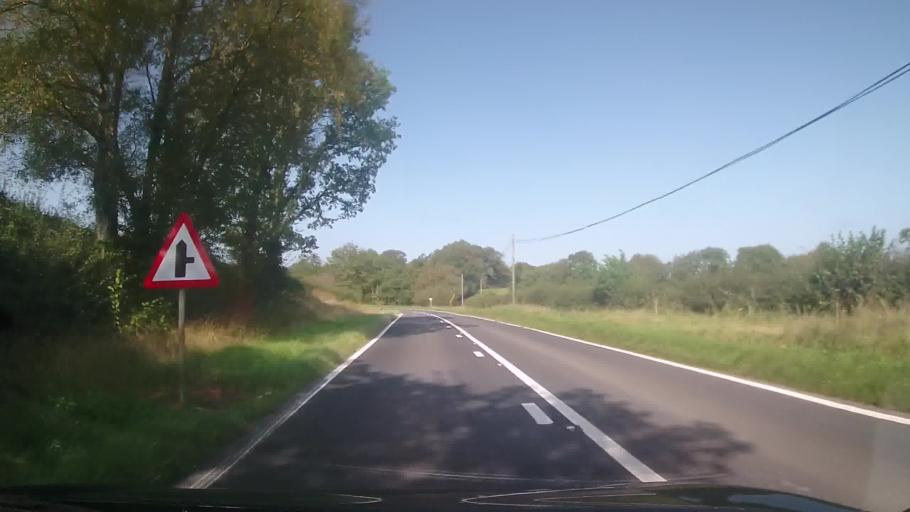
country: GB
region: Wales
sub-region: Sir Powys
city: Builth Wells
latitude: 52.1384
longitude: -3.5500
